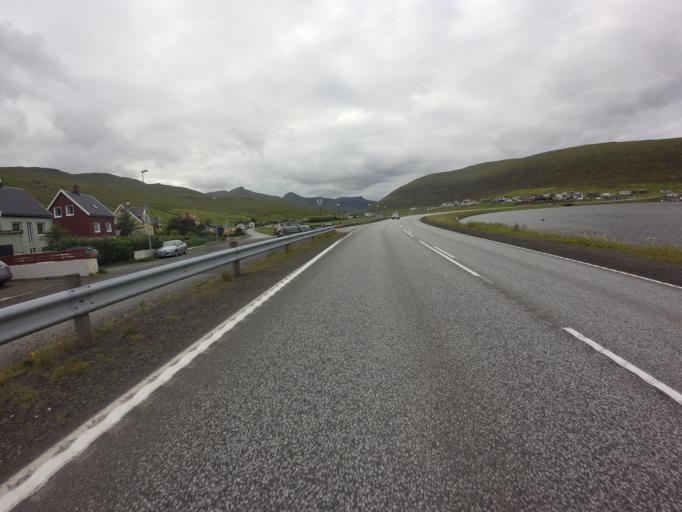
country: FO
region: Eysturoy
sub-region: Eidi
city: Eidi
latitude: 62.1851
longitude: -7.0248
